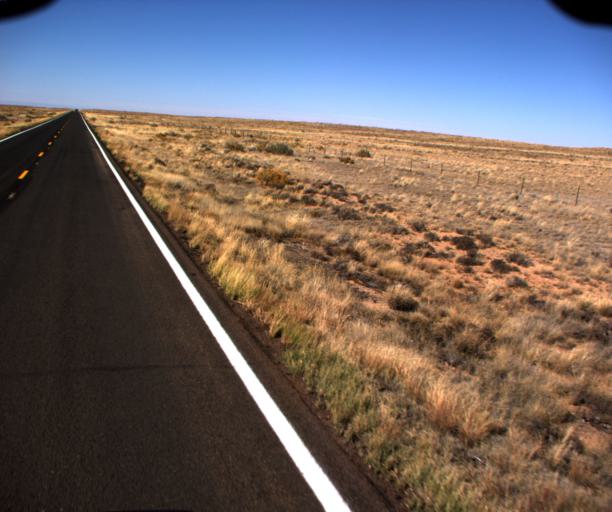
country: US
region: Arizona
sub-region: Coconino County
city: Tuba City
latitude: 35.9628
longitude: -110.9439
